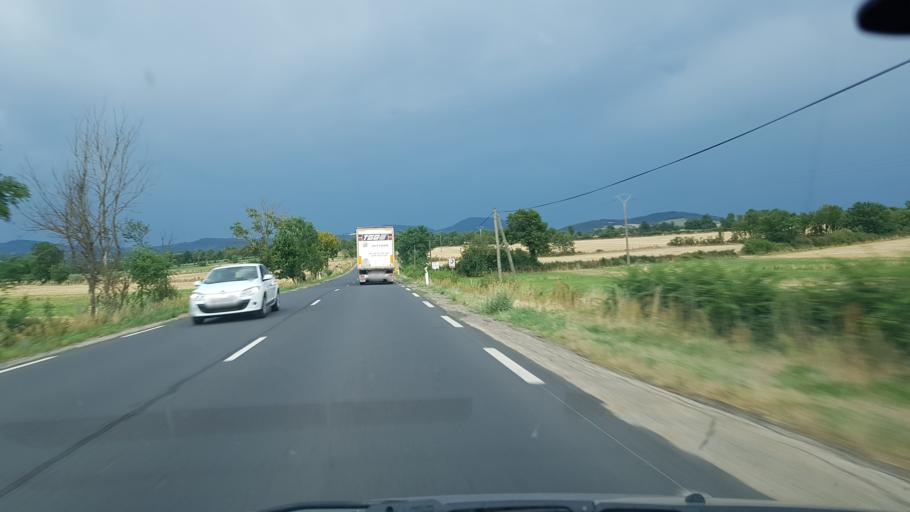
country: FR
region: Auvergne
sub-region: Departement de la Haute-Loire
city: Paulhaguet
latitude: 45.1696
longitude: 3.5272
